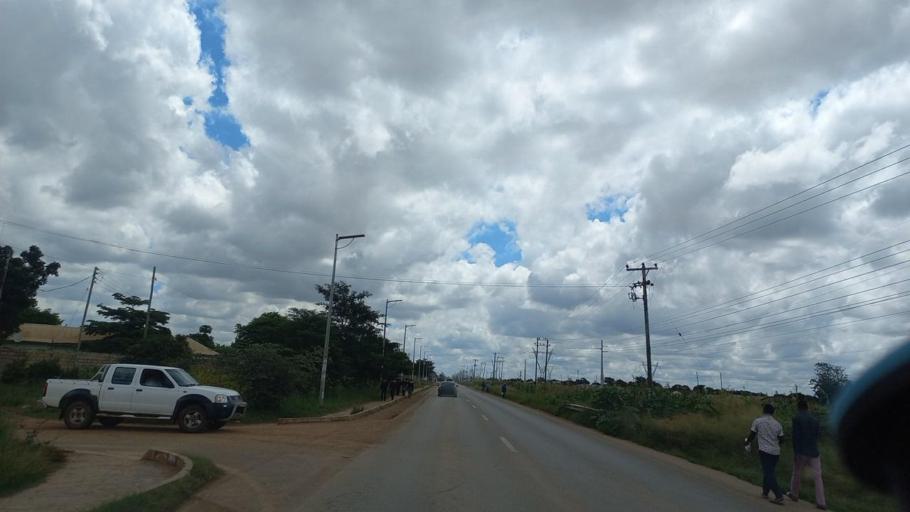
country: ZM
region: Lusaka
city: Lusaka
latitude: -15.4583
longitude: 28.3323
